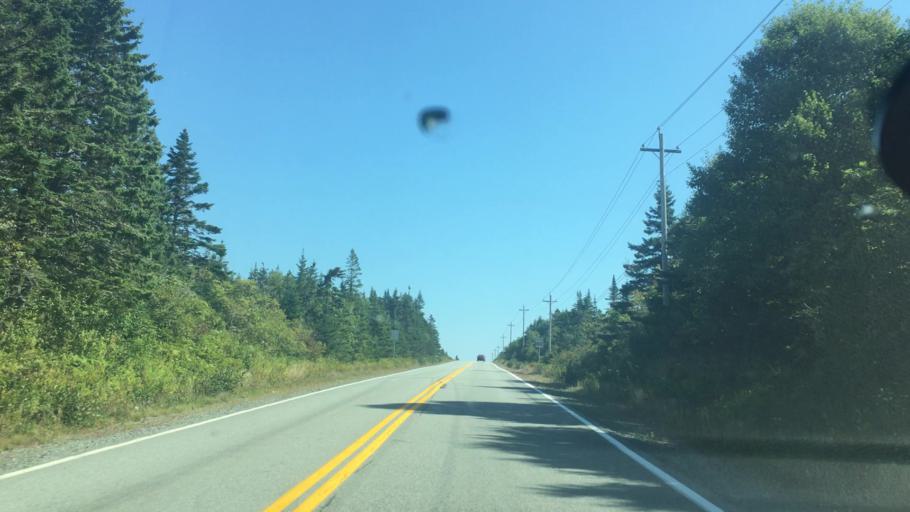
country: CA
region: Nova Scotia
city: Antigonish
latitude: 44.9324
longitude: -62.2883
